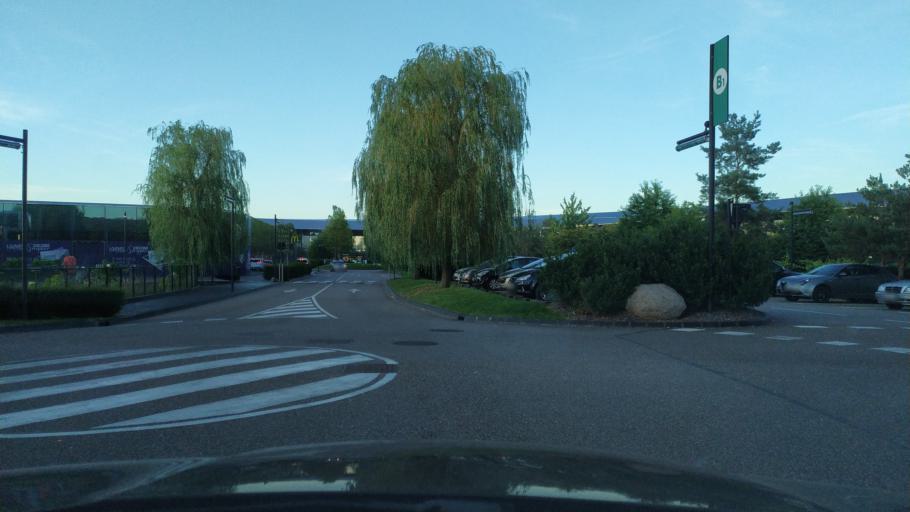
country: FR
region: Lorraine
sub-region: Departement de la Moselle
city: Moulins-les-Metz
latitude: 49.0814
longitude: 6.1031
